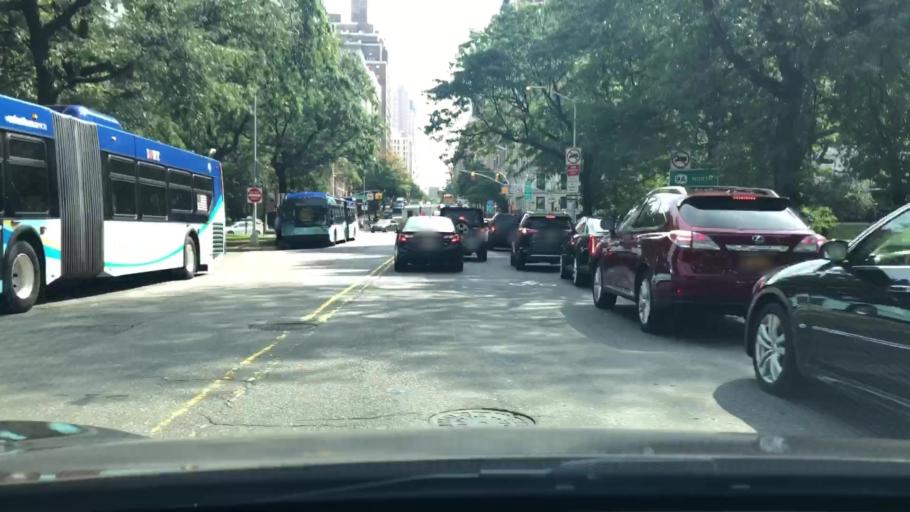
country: US
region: New York
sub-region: New York County
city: Manhattan
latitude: 40.7855
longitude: -73.9839
